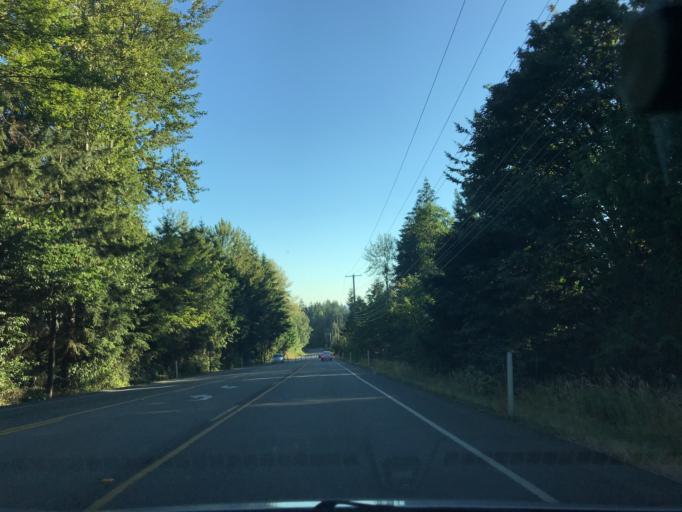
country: US
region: Washington
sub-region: Pierce County
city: Sumner
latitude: 47.2202
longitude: -122.2090
